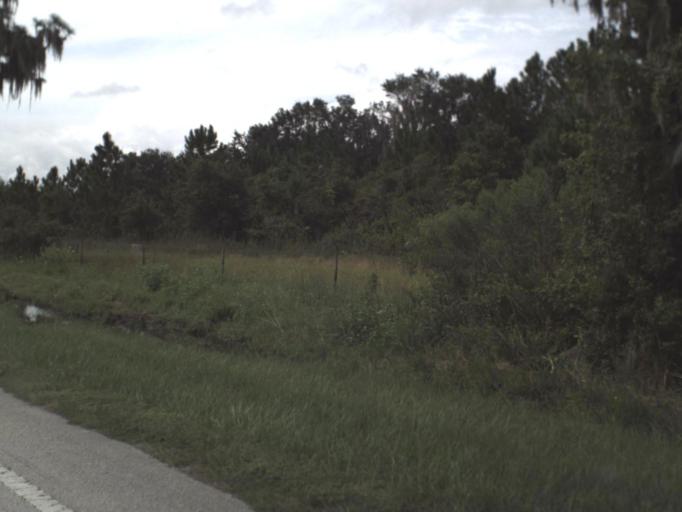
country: US
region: Florida
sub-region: Hillsborough County
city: Wimauma
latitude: 27.5898
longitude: -82.1160
